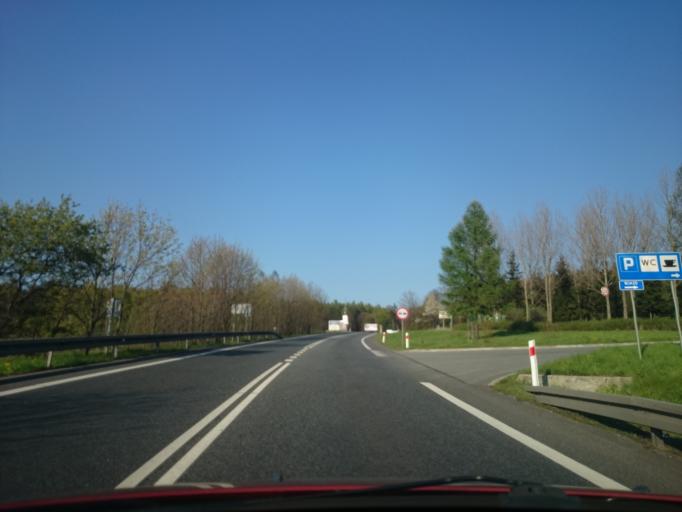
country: PL
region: Lower Silesian Voivodeship
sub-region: Powiat klodzki
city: Szczytna
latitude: 50.4224
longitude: 16.4579
